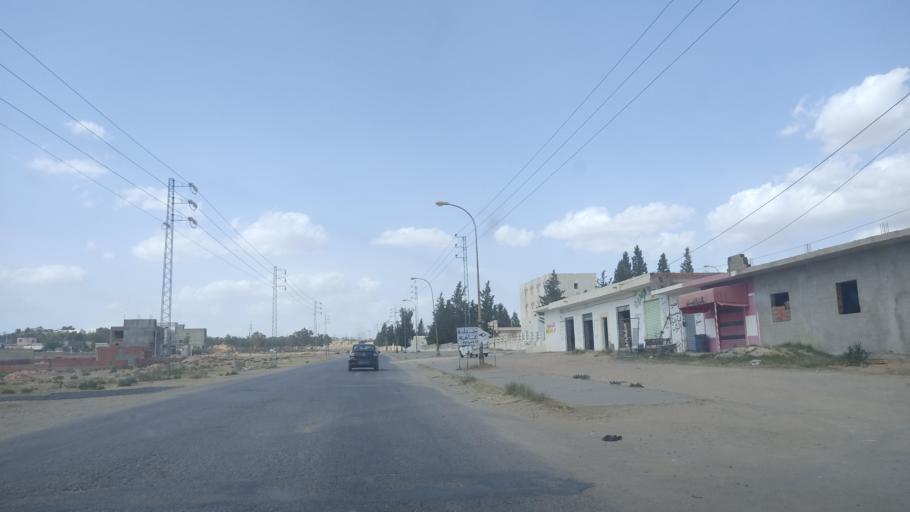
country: TN
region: Sidi Bu Zayd
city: Sidi Bouzid
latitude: 35.1033
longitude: 9.5356
